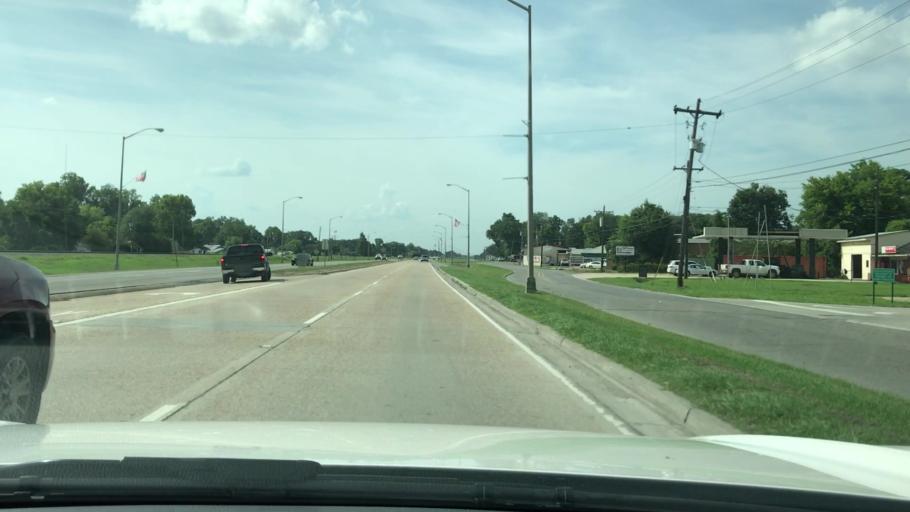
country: US
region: Louisiana
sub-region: Iberville Parish
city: Plaquemine
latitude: 30.2972
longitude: -91.2408
